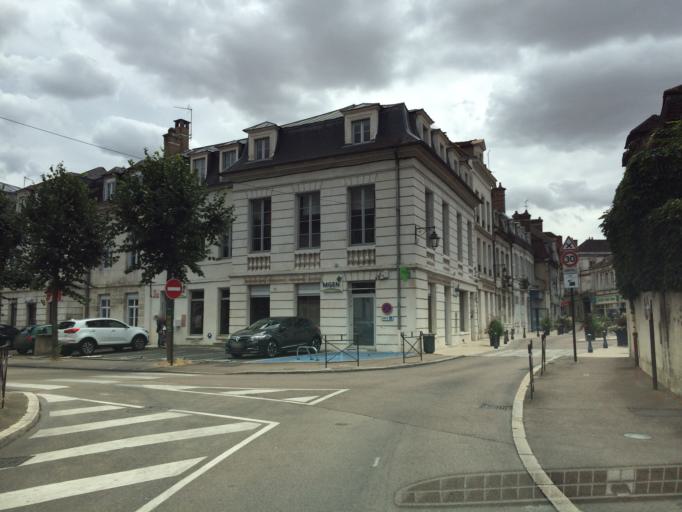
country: FR
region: Bourgogne
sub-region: Departement de l'Yonne
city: Auxerre
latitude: 47.7976
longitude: 3.5694
